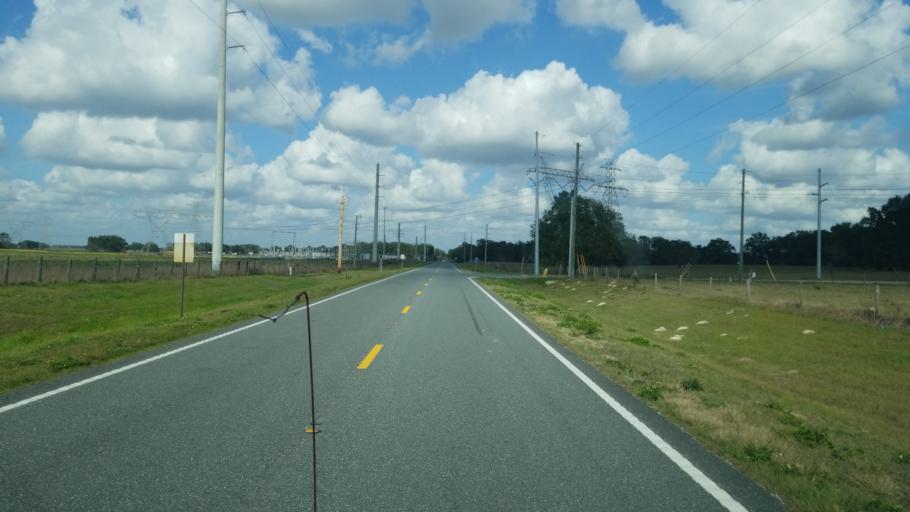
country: US
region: Florida
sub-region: Sumter County
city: Wildwood
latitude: 28.8937
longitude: -82.1200
